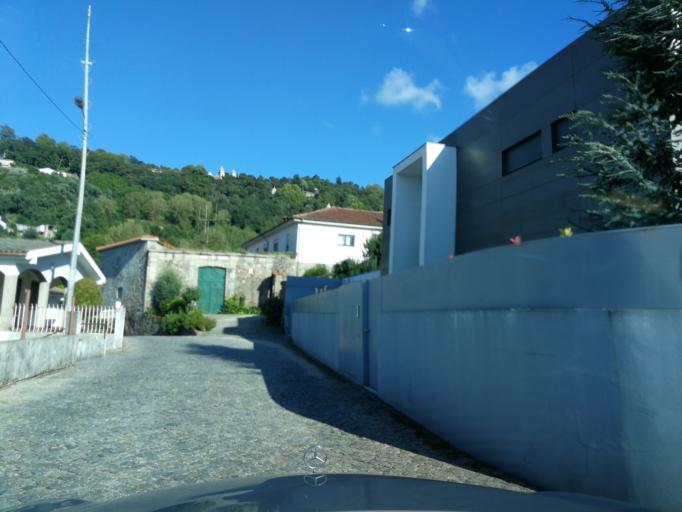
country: PT
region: Braga
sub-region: Braga
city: Adaufe
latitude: 41.5571
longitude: -8.3851
